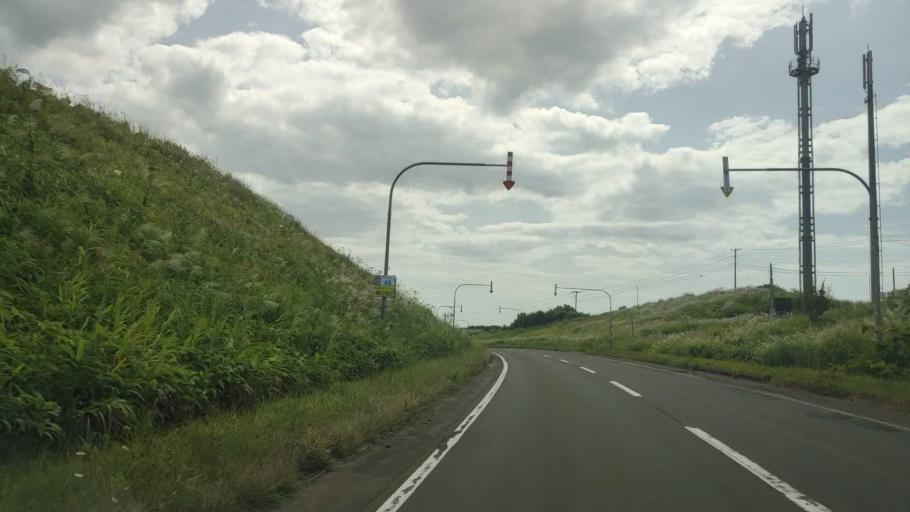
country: JP
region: Hokkaido
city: Rumoi
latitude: 44.6012
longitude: 141.7919
